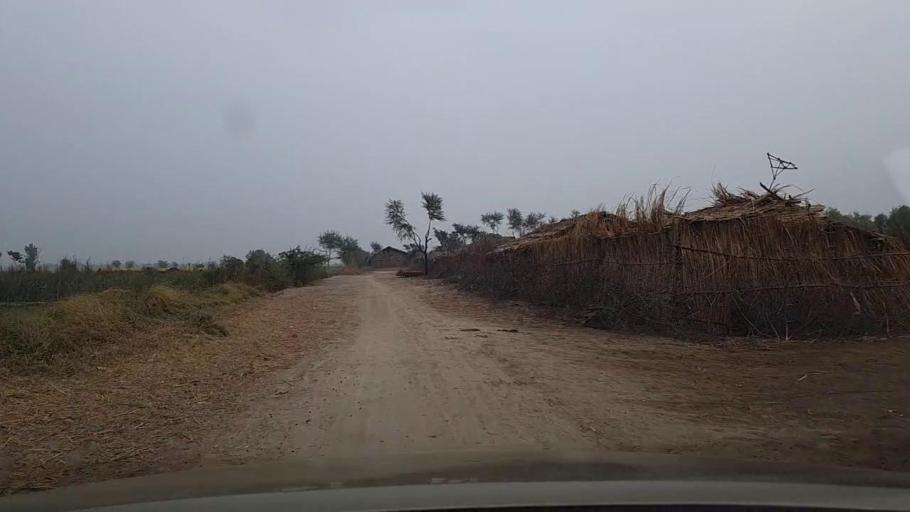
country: PK
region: Sindh
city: Sanghar
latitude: 26.1189
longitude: 68.9214
